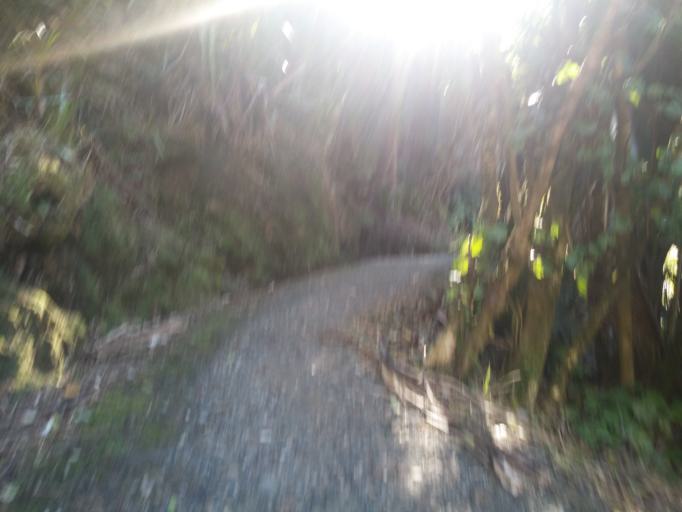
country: NZ
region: West Coast
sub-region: Grey District
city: Greymouth
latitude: -42.1091
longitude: 171.3421
